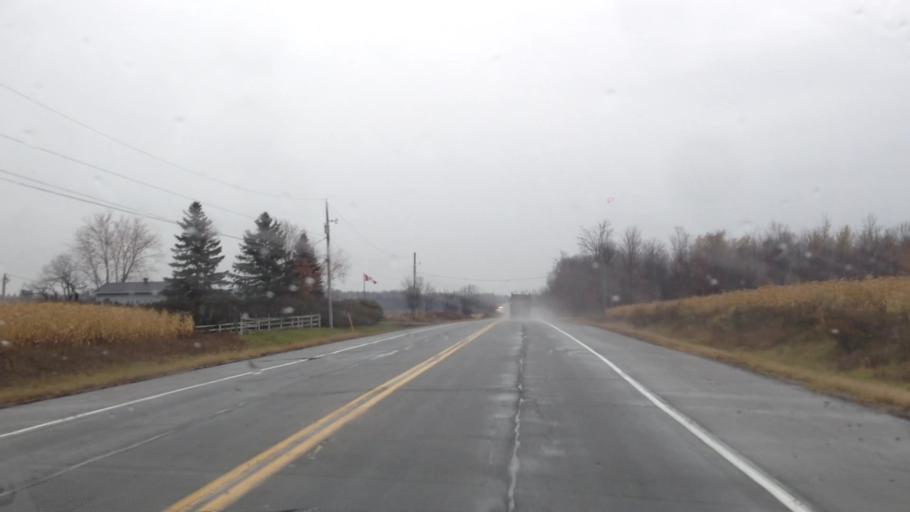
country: CA
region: Ontario
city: Clarence-Rockland
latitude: 45.3931
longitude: -75.3921
